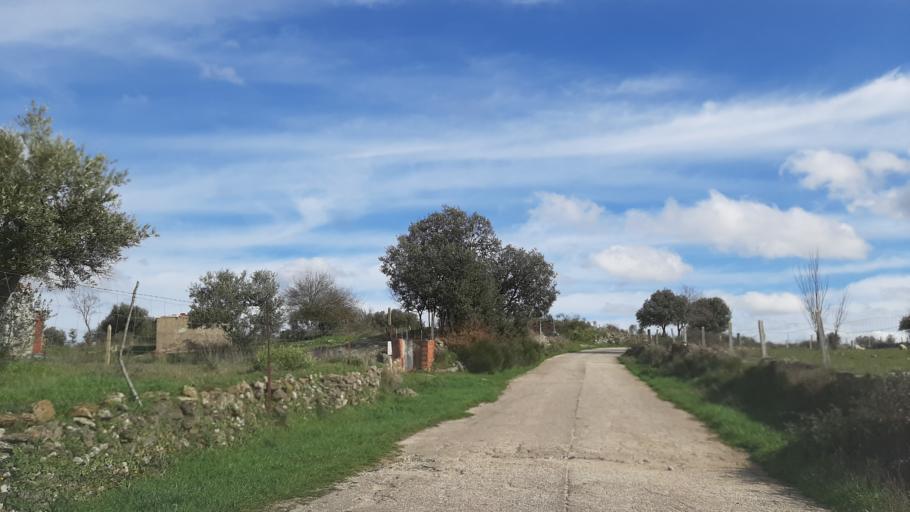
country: ES
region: Castille and Leon
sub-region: Provincia de Salamanca
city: Villarino de los Aires
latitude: 41.2536
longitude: -6.5247
